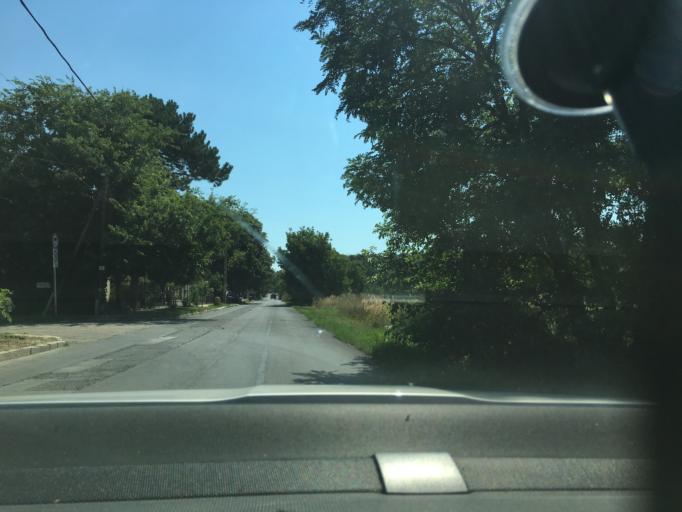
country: HU
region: Budapest
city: Budapest XVI. keruelet
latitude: 47.5008
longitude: 19.1788
